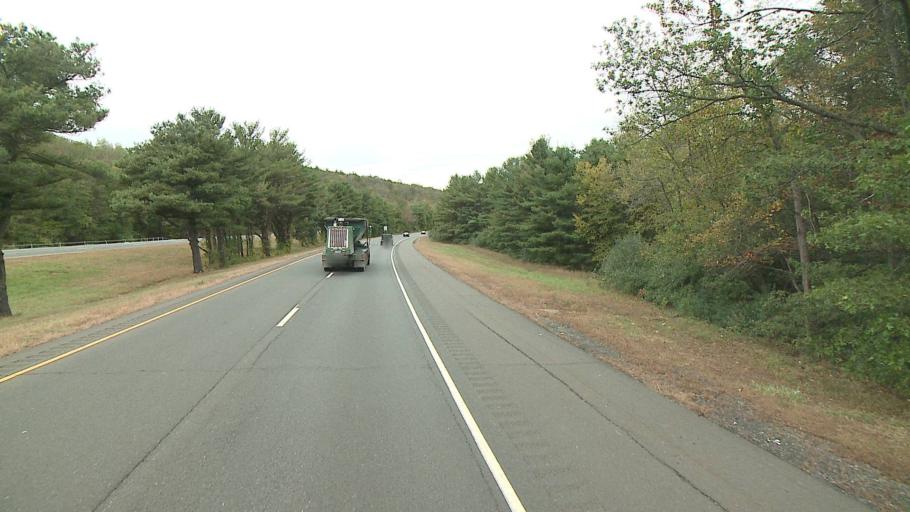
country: US
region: Connecticut
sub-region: Middlesex County
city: Higganum
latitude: 41.4726
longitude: -72.5574
